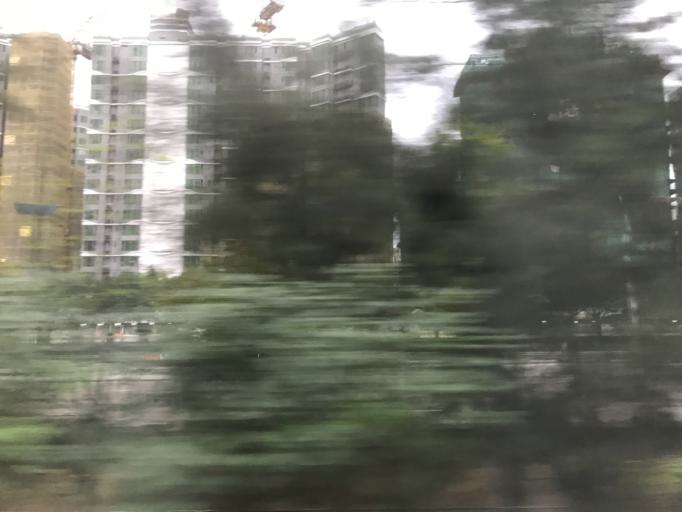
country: HK
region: Tai Po
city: Tai Po
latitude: 22.4280
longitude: 114.2045
